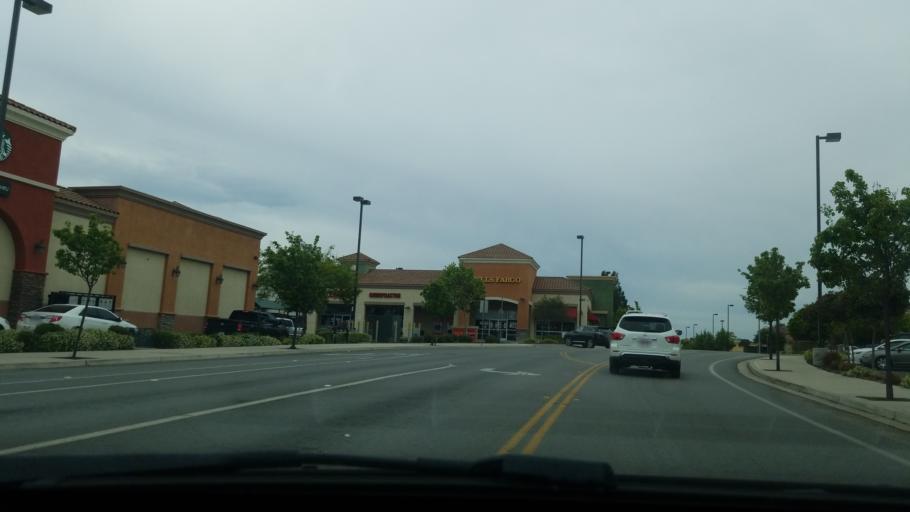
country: US
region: California
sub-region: San Luis Obispo County
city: Nipomo
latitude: 35.0355
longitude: -120.4865
